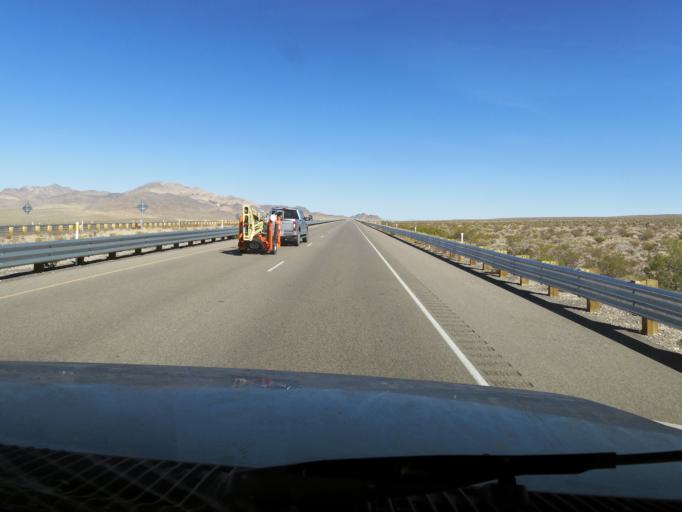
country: US
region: Nevada
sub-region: Nye County
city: Pahrump
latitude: 36.5965
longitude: -116.0072
